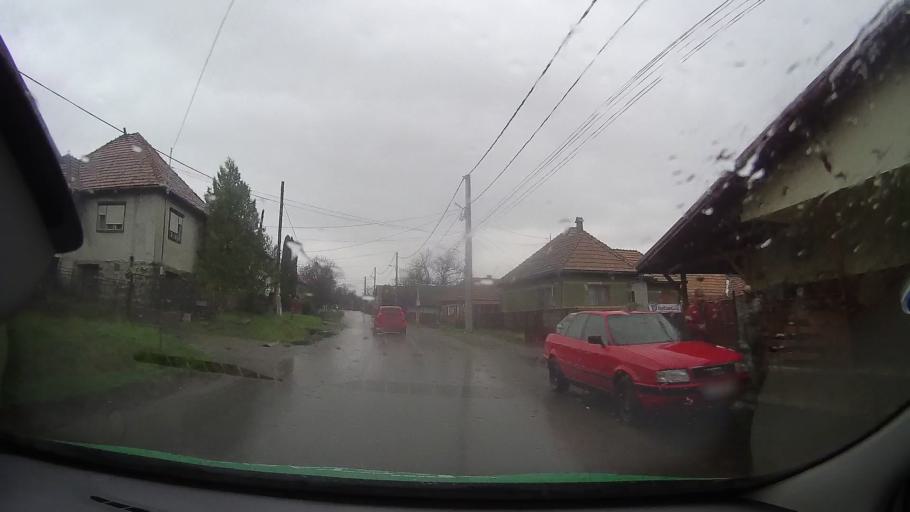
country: RO
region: Mures
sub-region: Comuna Vatava
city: Vatava
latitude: 46.9369
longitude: 24.7679
